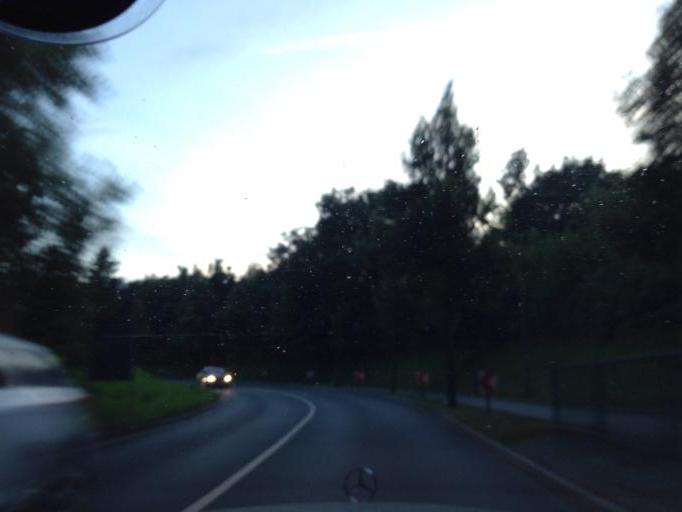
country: DE
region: Schleswig-Holstein
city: Ahrensburg
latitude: 53.6767
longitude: 10.2467
